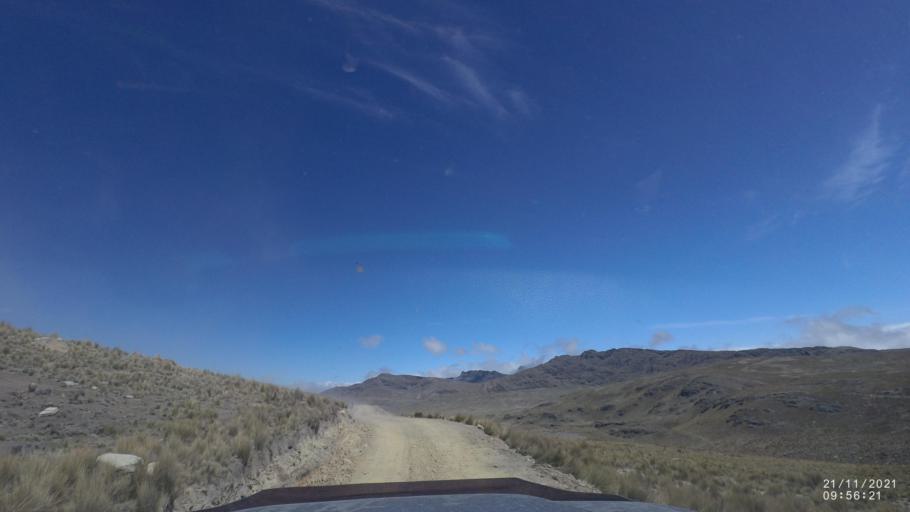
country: BO
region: Cochabamba
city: Cochabamba
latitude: -17.0421
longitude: -66.2657
